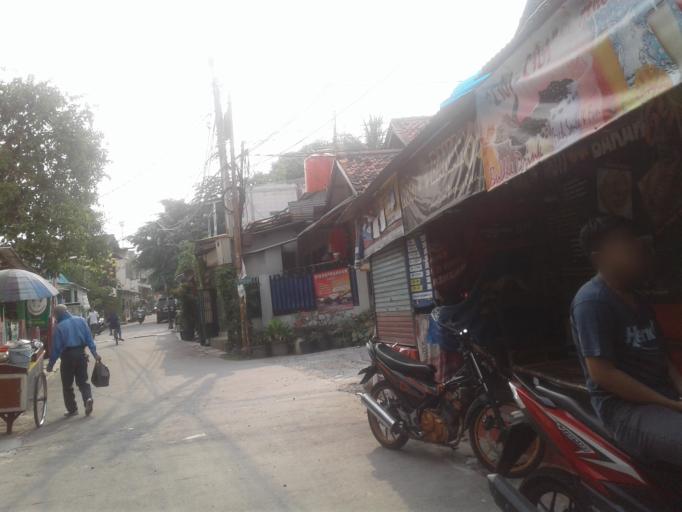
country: ID
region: West Java
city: Depok
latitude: -6.3689
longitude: 106.8366
